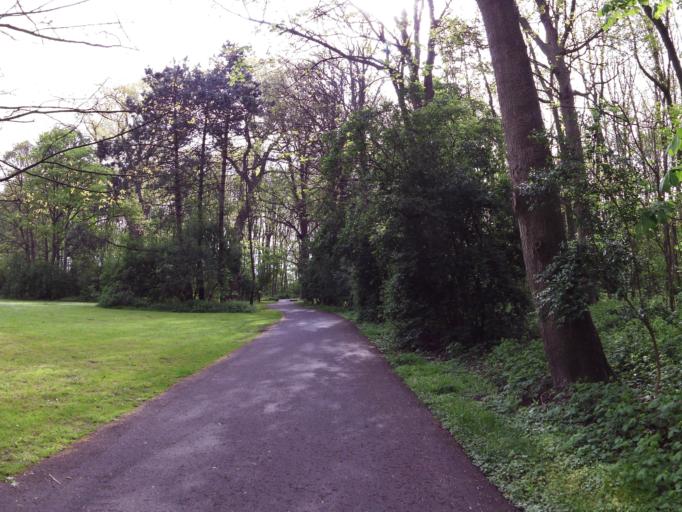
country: BE
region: Flanders
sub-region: Provincie West-Vlaanderen
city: Ostend
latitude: 51.2207
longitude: 2.9293
